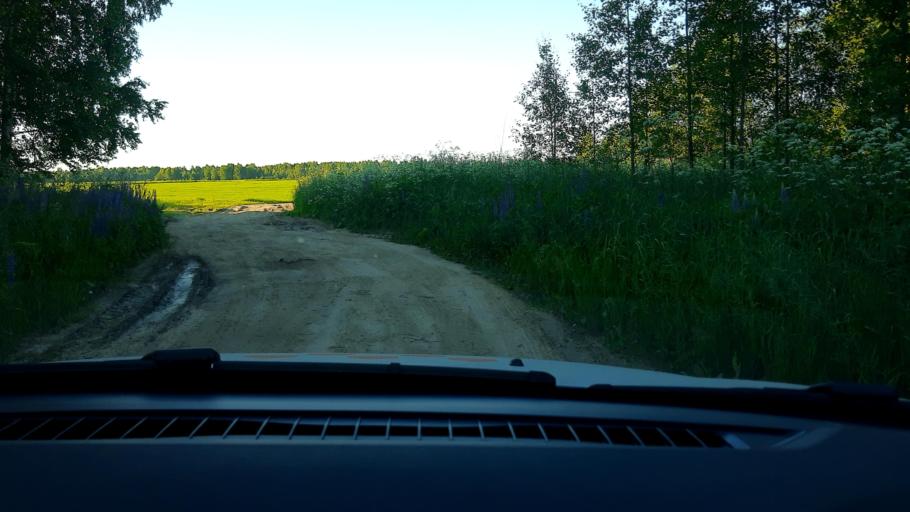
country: RU
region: Nizjnij Novgorod
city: Kstovo
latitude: 56.3022
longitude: 44.2576
